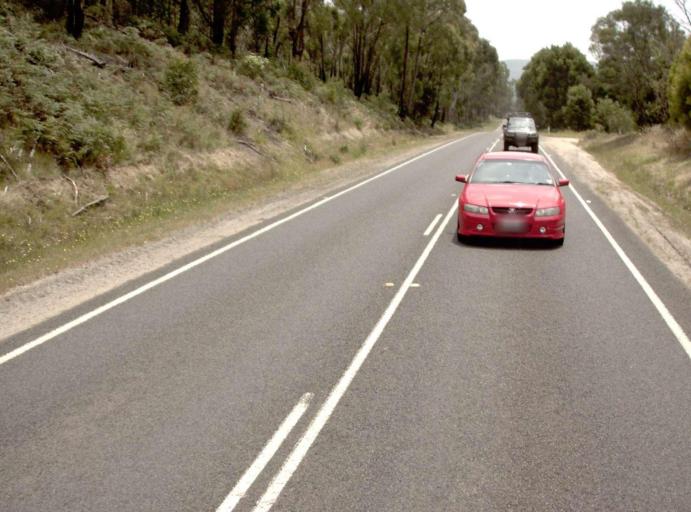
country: AU
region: Victoria
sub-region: Latrobe
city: Traralgon
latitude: -38.4484
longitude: 146.7358
